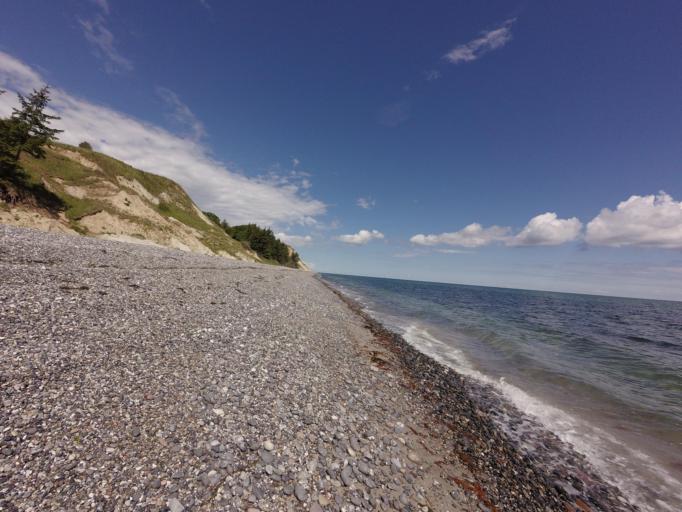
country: DK
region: Central Jutland
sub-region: Norddjurs Kommune
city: Grenaa
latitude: 56.5101
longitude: 10.8671
